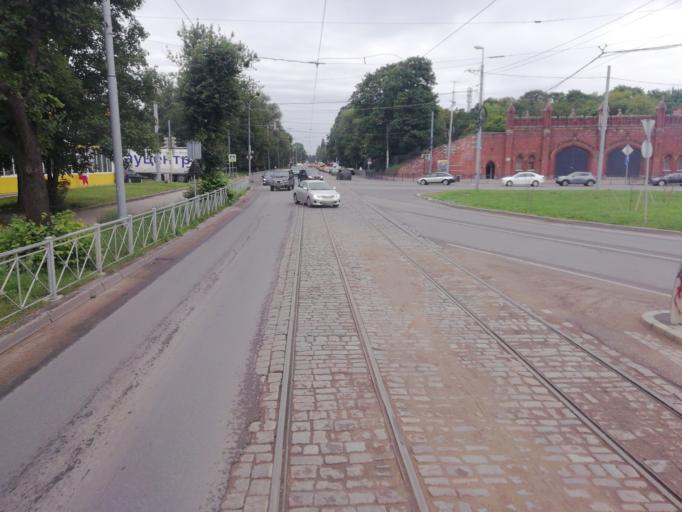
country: RU
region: Kaliningrad
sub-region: Gorod Kaliningrad
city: Kaliningrad
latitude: 54.6961
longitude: 20.5214
